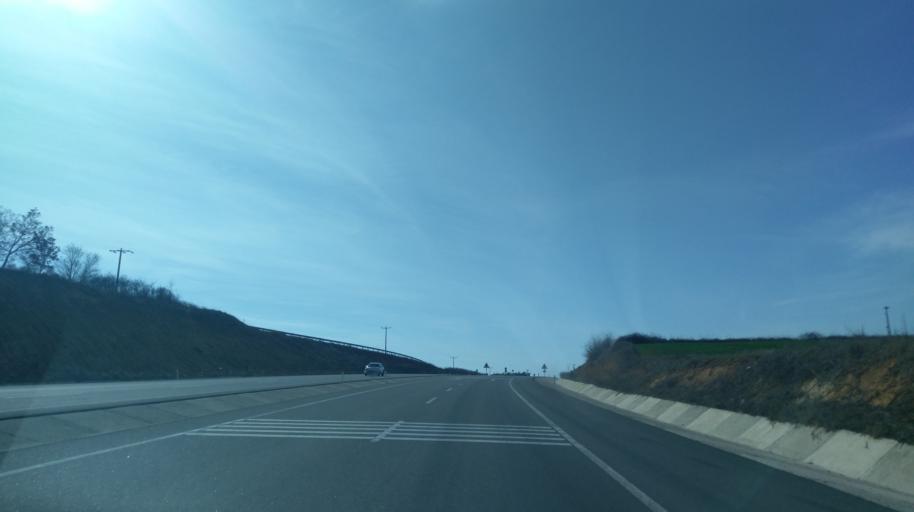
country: TR
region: Edirne
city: Kesan
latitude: 40.9721
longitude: 26.6390
